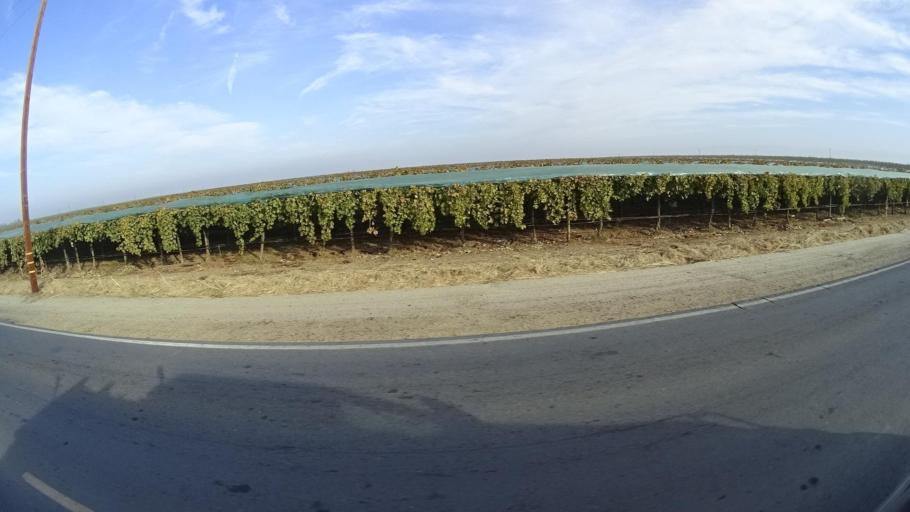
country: US
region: California
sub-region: Kern County
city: Delano
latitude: 35.7905
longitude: -119.2089
